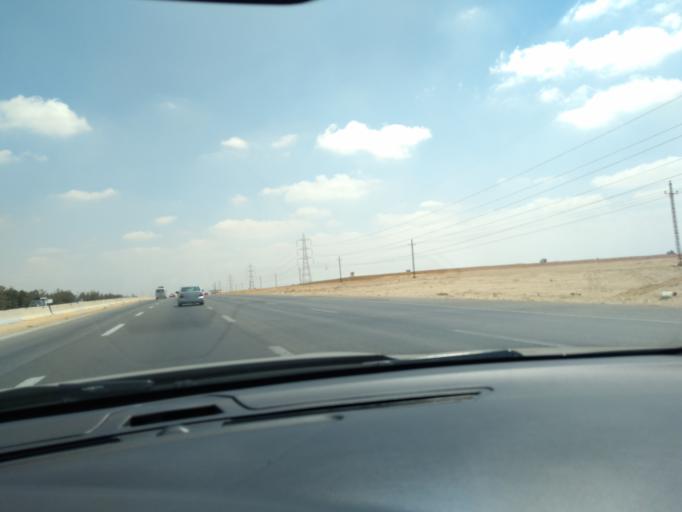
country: EG
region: Al Isma'iliyah
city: At Tall al Kabir
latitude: 30.3951
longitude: 31.9748
